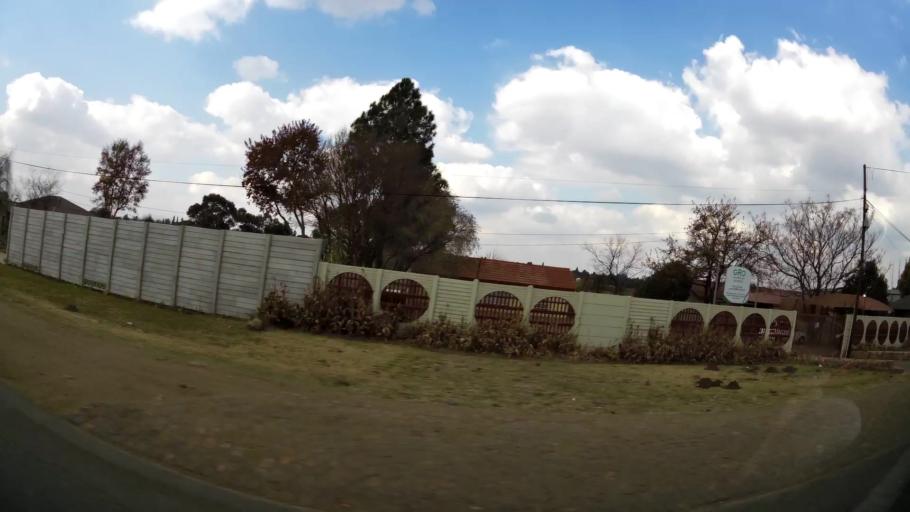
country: ZA
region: Gauteng
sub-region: Ekurhuleni Metropolitan Municipality
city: Benoni
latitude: -26.1231
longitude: 28.3581
